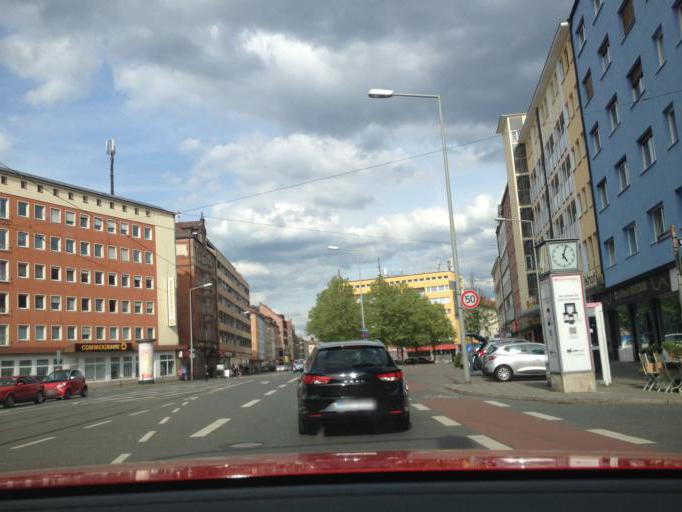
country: DE
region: Bavaria
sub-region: Regierungsbezirk Mittelfranken
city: Nuernberg
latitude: 49.4585
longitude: 11.0956
